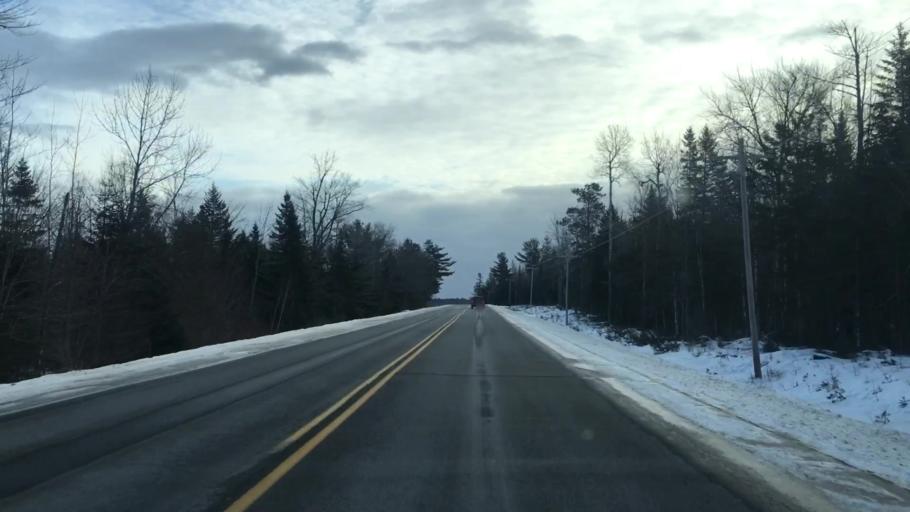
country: US
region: Maine
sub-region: Washington County
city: Machias
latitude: 44.9997
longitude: -67.5959
